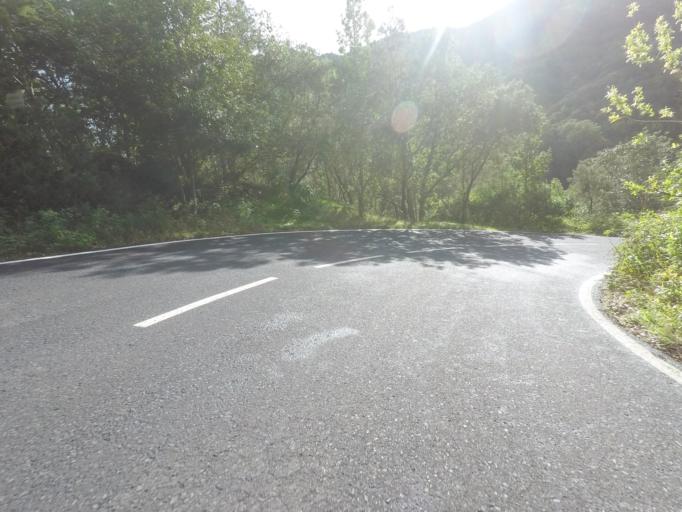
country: ES
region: Canary Islands
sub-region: Provincia de Santa Cruz de Tenerife
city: Hermigua
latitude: 28.1289
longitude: -17.2103
